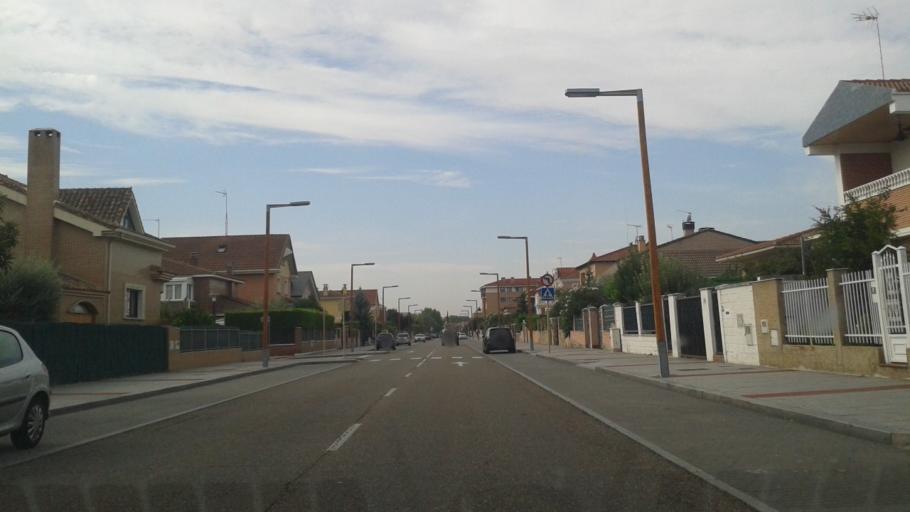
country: ES
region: Castille and Leon
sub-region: Provincia de Valladolid
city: Arroyo
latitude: 41.6168
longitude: -4.7829
